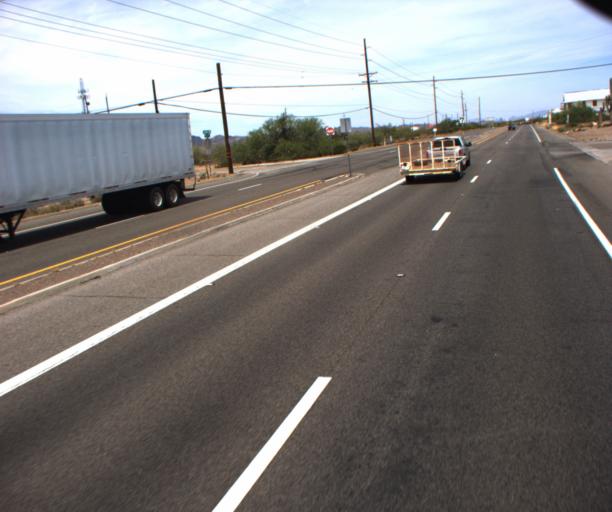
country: US
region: Arizona
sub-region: Maricopa County
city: Wickenburg
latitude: 33.8542
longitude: -112.6230
